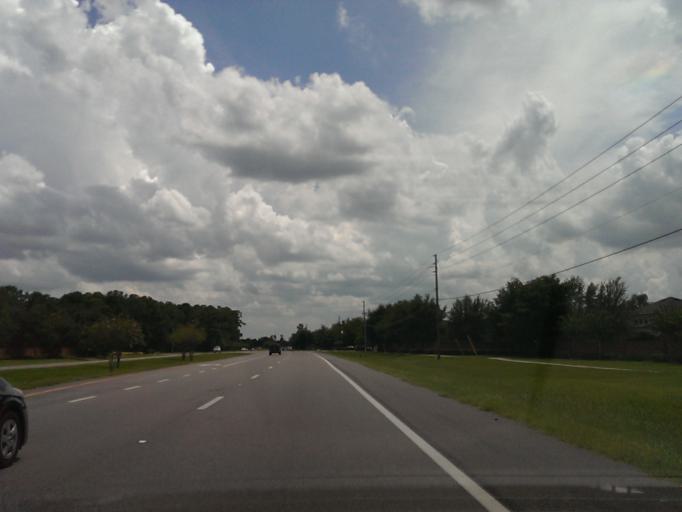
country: US
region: Florida
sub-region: Orange County
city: Bay Hill
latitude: 28.4257
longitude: -81.5331
